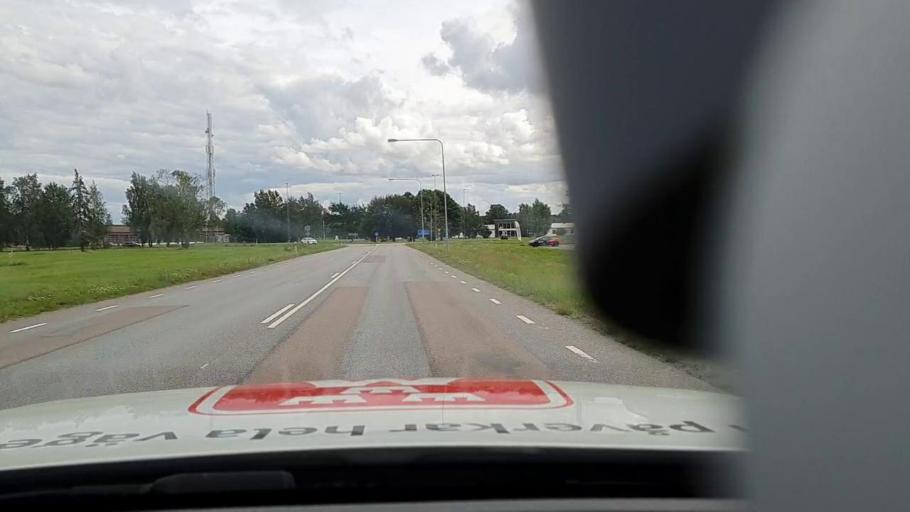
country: SE
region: Vaestra Goetaland
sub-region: Lidkopings Kommun
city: Lidkoping
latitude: 58.5045
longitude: 13.1241
